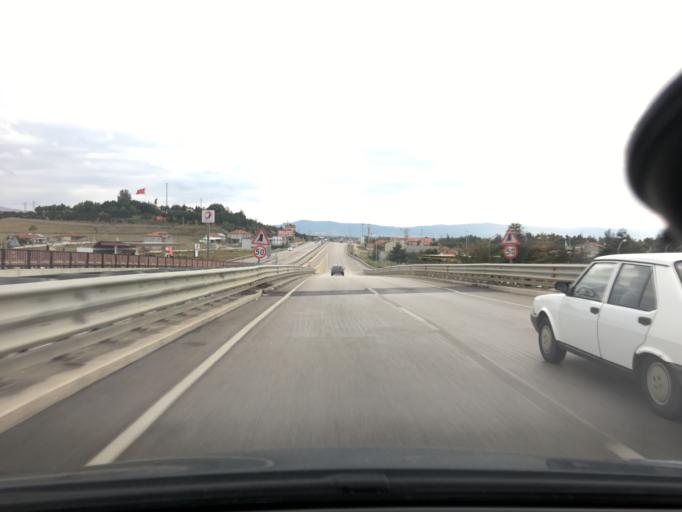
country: TR
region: Afyonkarahisar
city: Sincanli
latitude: 38.7962
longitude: 30.3891
